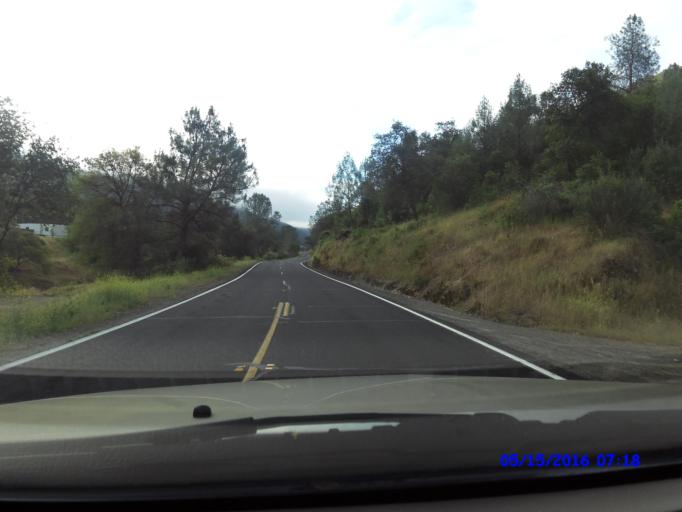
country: US
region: California
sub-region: Tuolumne County
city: Tuolumne City
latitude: 37.8076
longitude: -120.2987
